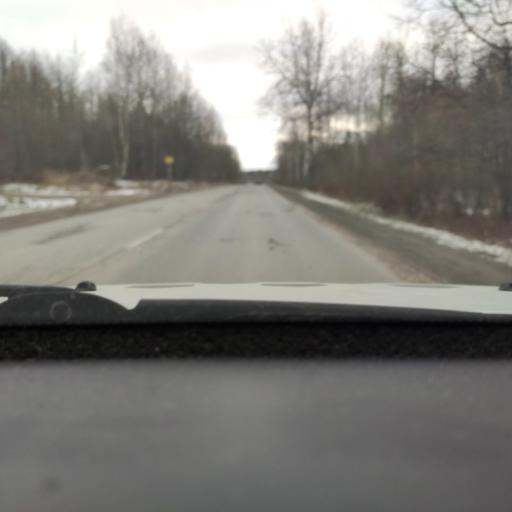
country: RU
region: Perm
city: Perm
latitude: 58.0983
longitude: 56.4075
